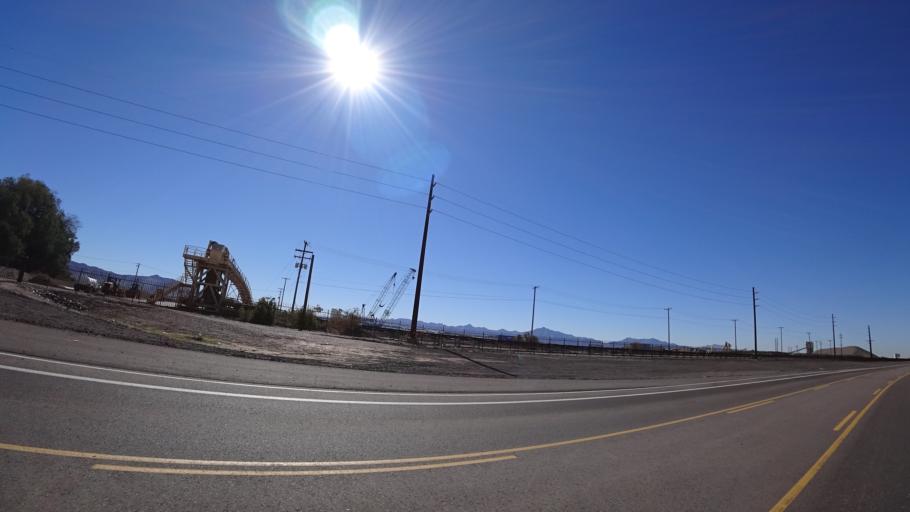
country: US
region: Arizona
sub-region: Maricopa County
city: Laveen
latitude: 33.4034
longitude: -112.1523
